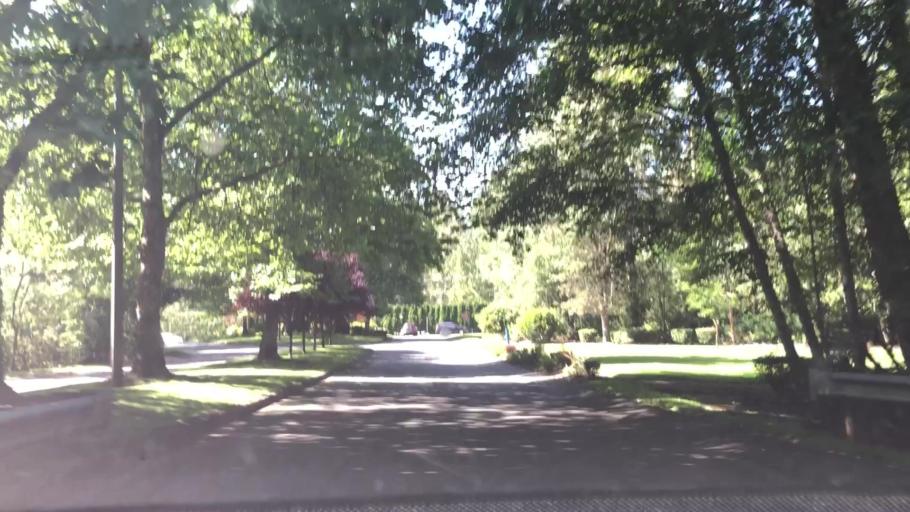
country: US
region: Washington
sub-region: King County
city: Cottage Lake
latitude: 47.7166
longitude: -122.0749
